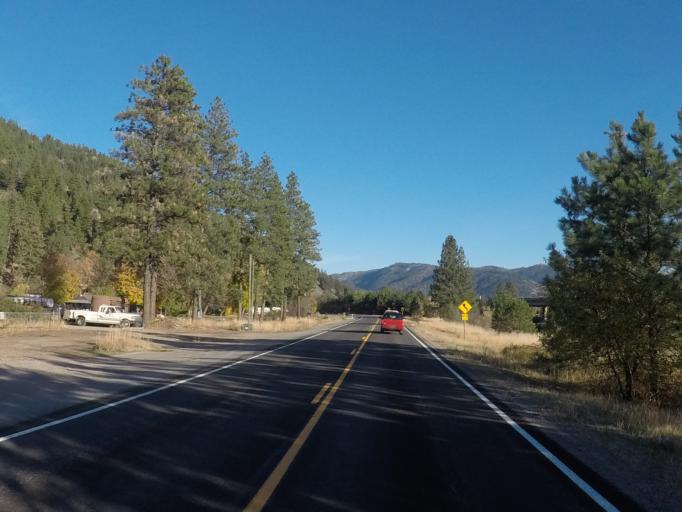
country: US
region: Montana
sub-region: Missoula County
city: Clinton
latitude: 46.7965
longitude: -113.7531
